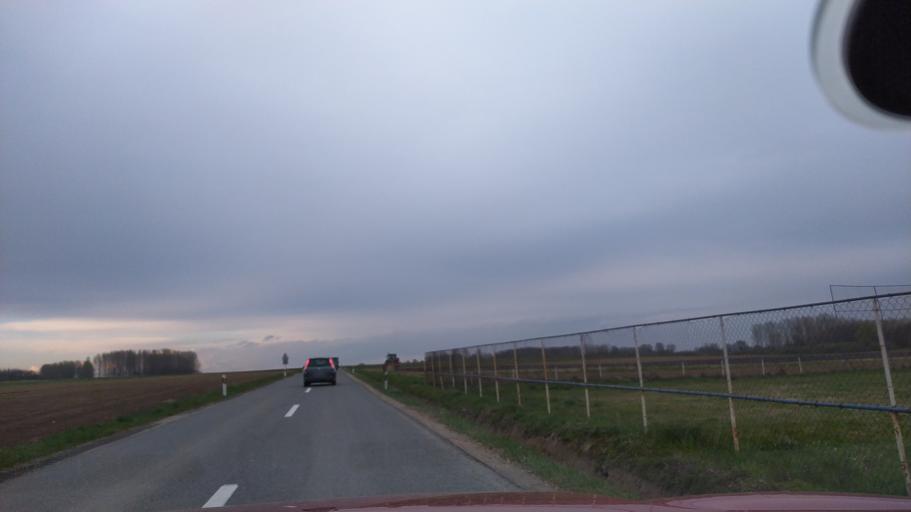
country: HR
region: Varazdinska
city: Ludbreg
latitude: 46.2421
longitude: 16.5527
